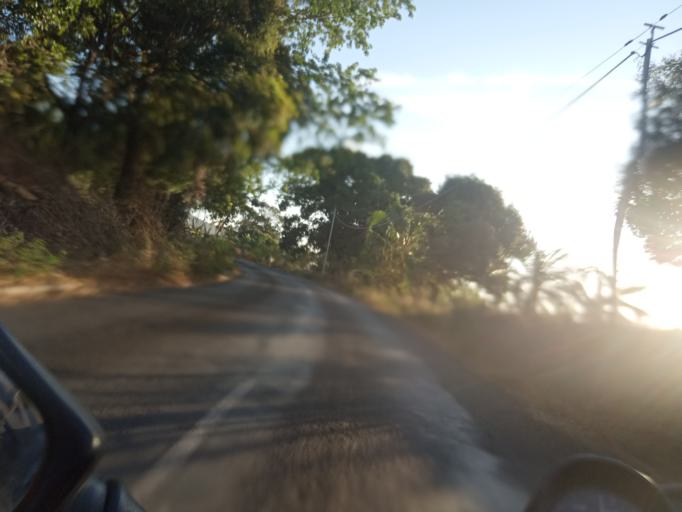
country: YT
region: Kani-Keli
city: Kani Keli
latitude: -12.9369
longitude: 45.1024
